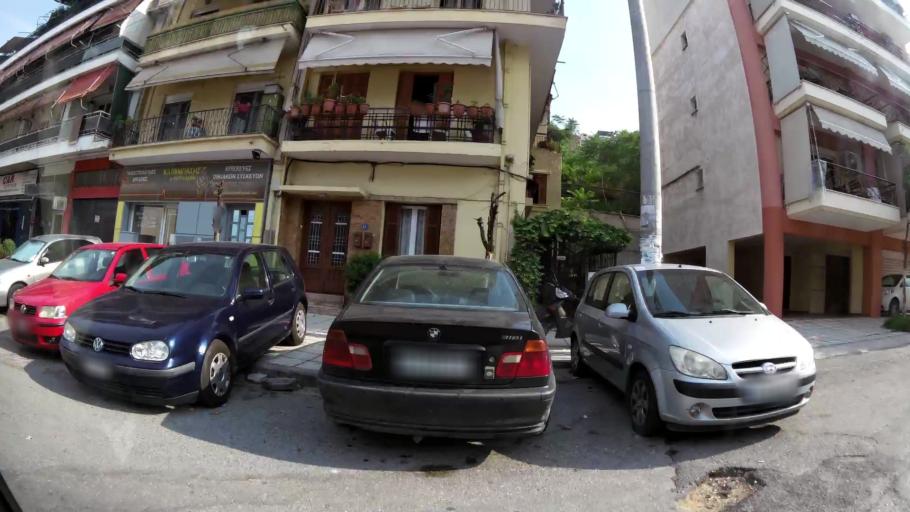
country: GR
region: Central Macedonia
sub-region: Nomos Thessalonikis
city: Sykies
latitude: 40.6457
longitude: 22.9442
